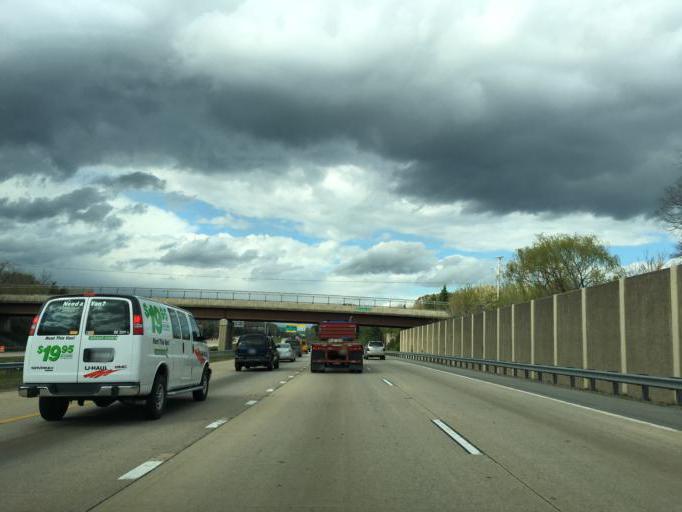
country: US
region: Maryland
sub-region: Anne Arundel County
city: Ferndale
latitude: 39.1841
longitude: -76.6322
